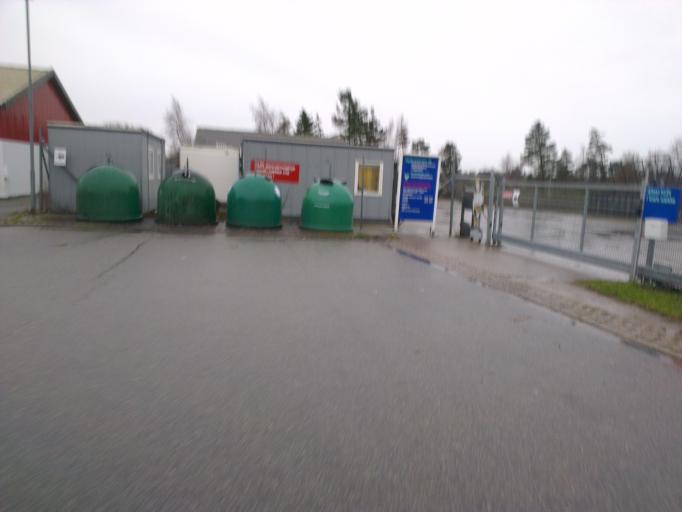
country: DK
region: Capital Region
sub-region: Frederikssund Kommune
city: Jaegerspris
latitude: 55.8306
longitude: 11.9930
